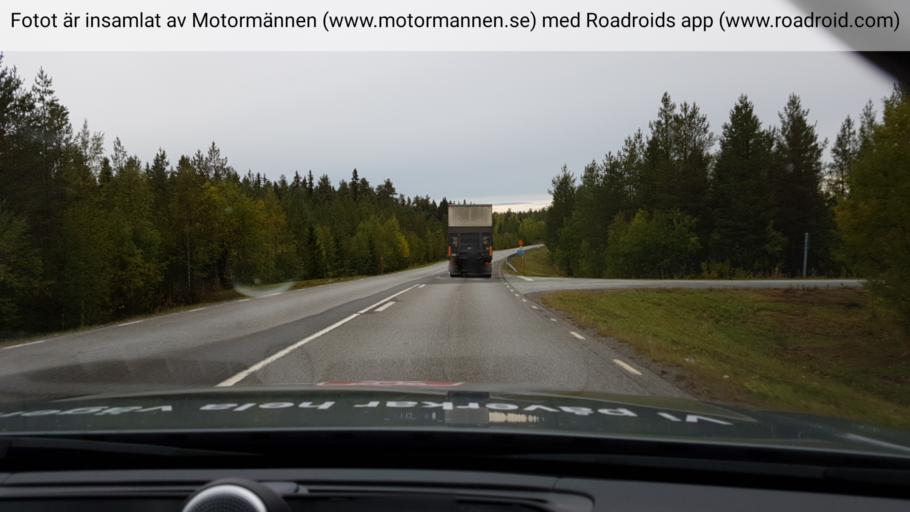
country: SE
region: Jaemtland
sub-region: Stroemsunds Kommun
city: Stroemsund
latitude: 64.2384
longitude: 15.4547
